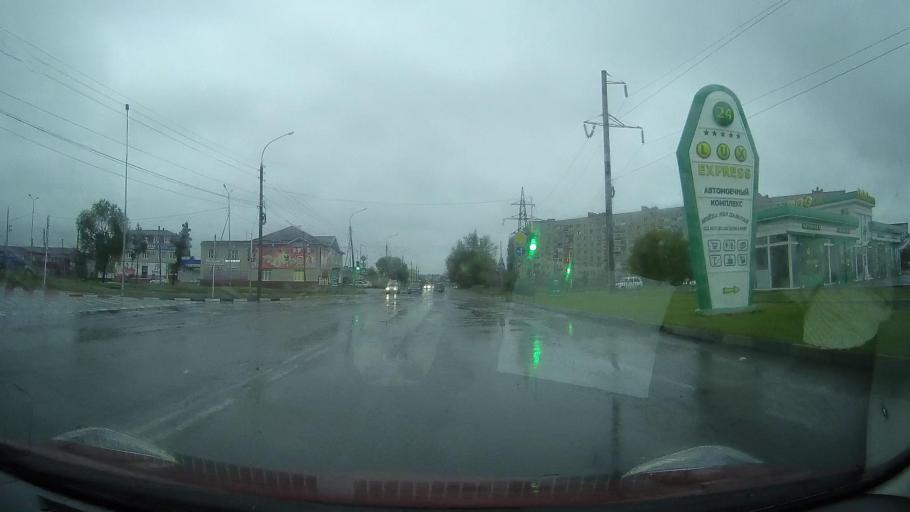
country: RU
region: Stavropol'skiy
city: Nevinnomyssk
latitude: 44.6406
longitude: 41.9589
